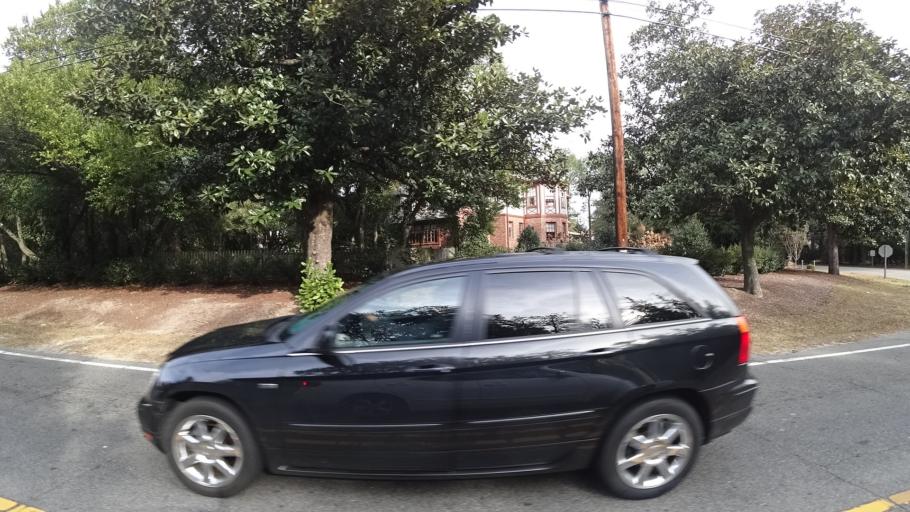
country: US
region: North Carolina
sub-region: Moore County
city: Pinehurst
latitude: 35.1931
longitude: -79.4735
